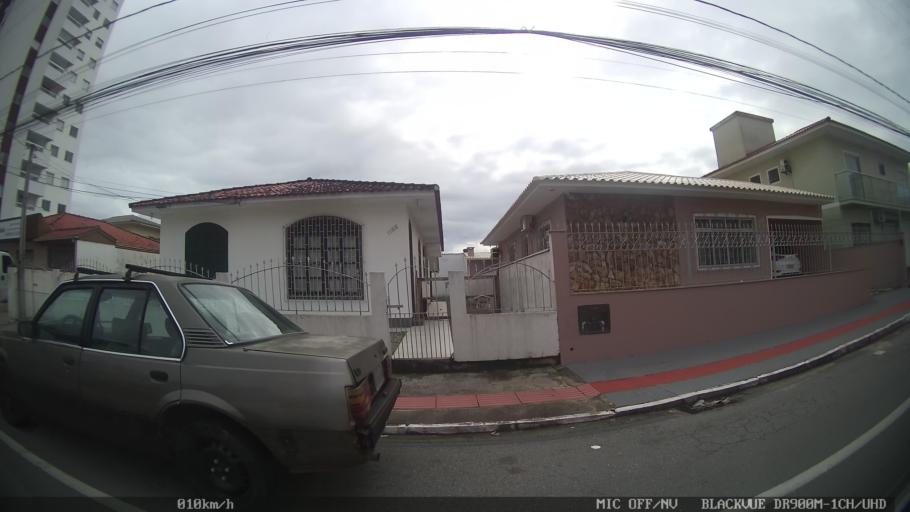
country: BR
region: Santa Catarina
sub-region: Sao Jose
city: Campinas
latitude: -27.5560
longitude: -48.6264
